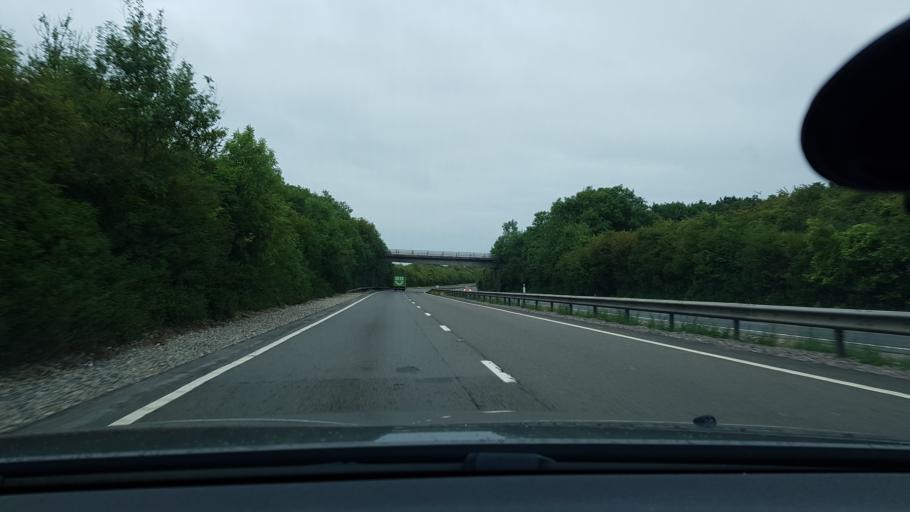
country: GB
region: England
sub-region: Hampshire
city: Overton
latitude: 51.2497
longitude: -1.3406
